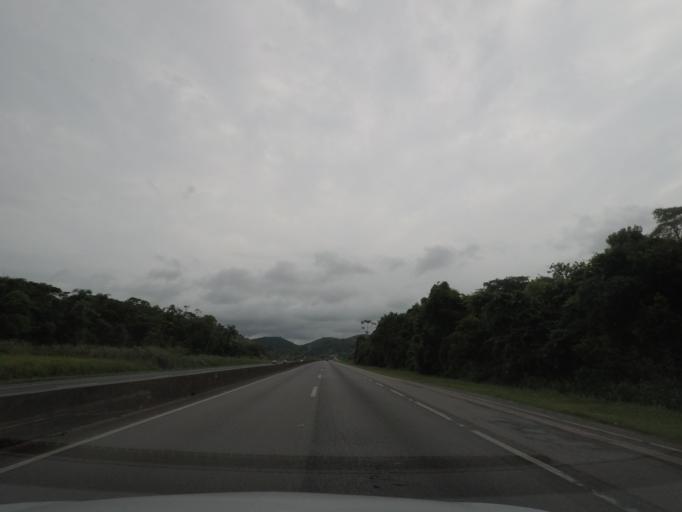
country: BR
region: Sao Paulo
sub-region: Juquia
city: Juquia
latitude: -24.3440
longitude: -47.6478
